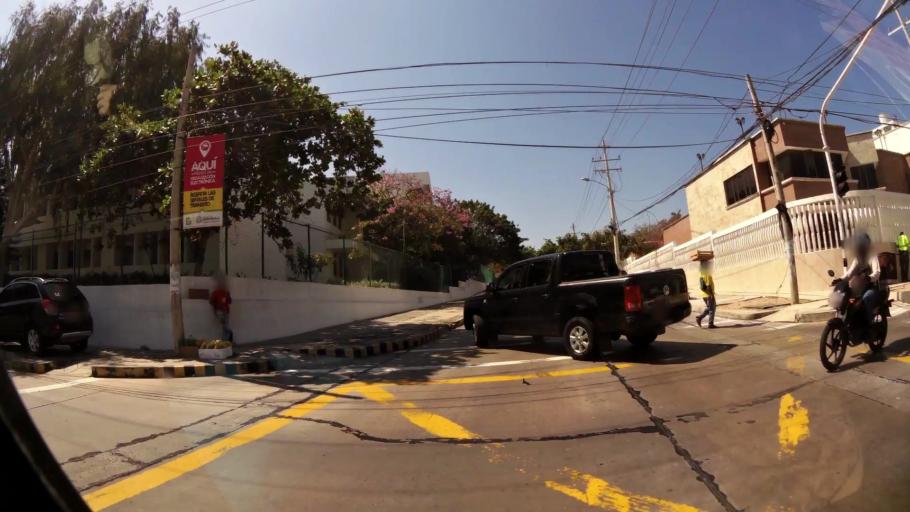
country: CO
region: Atlantico
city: Barranquilla
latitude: 11.0122
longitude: -74.8137
